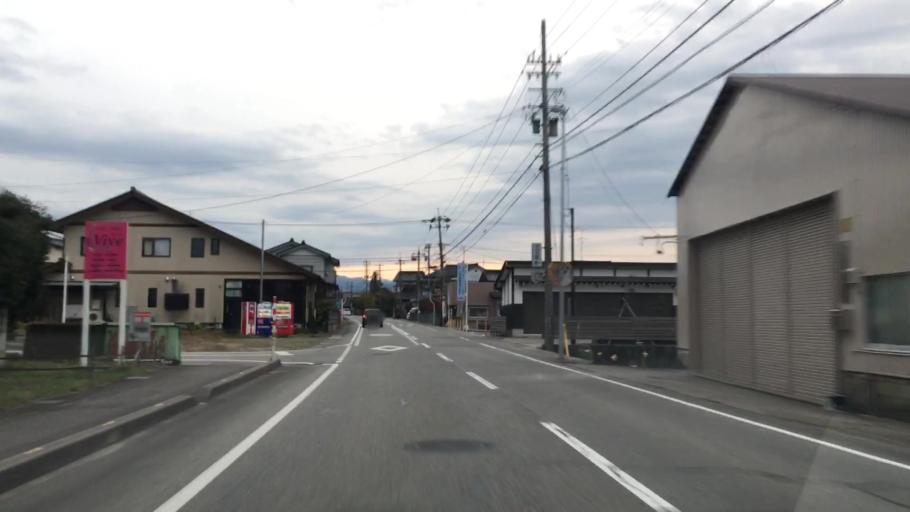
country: JP
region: Toyama
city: Kamiichi
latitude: 36.6990
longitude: 137.3152
